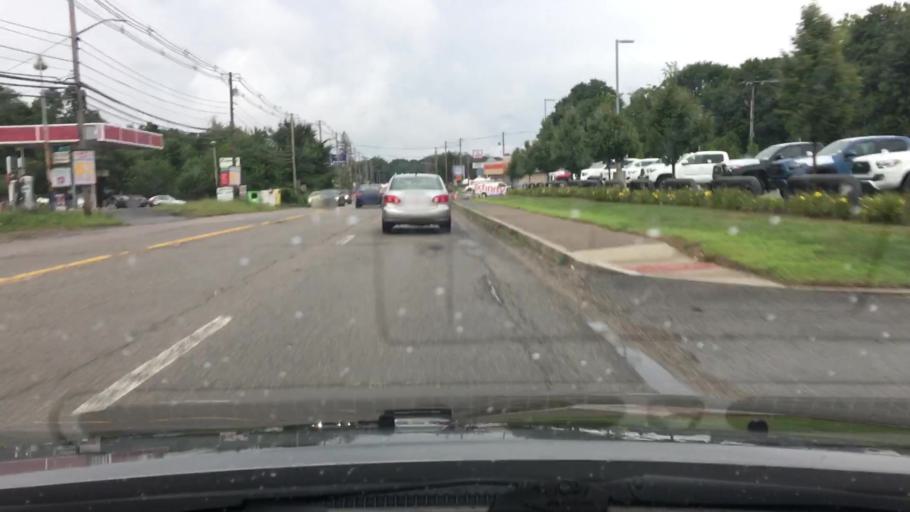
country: US
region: Massachusetts
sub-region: Norfolk County
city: Plainville
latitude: 41.9625
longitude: -71.3405
